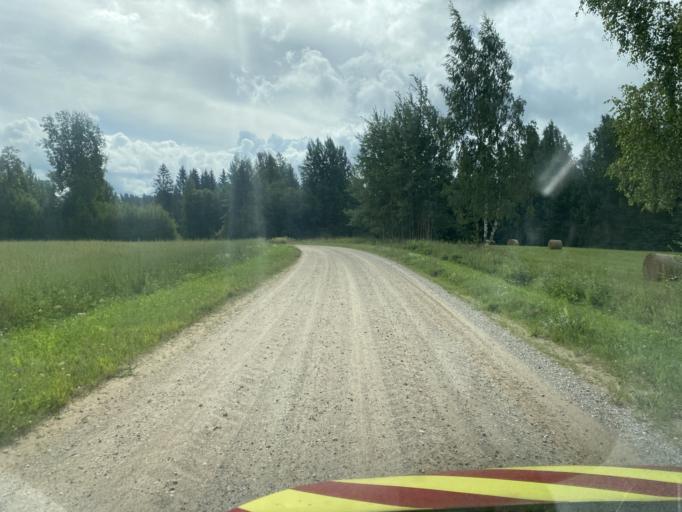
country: EE
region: Viljandimaa
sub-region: Karksi vald
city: Karksi-Nuia
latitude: 58.0611
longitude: 25.5345
